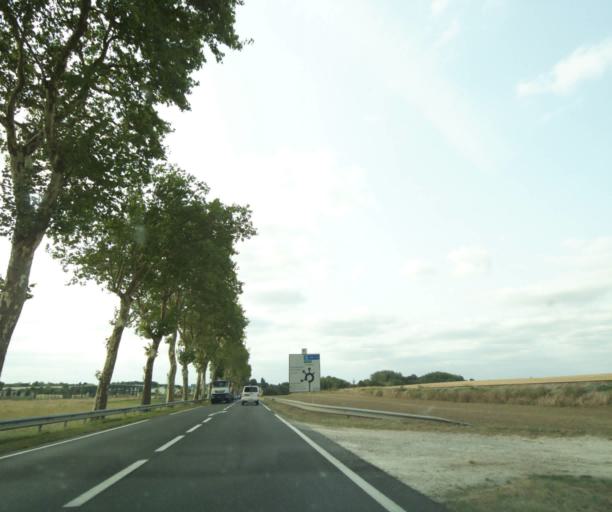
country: FR
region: Centre
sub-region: Departement d'Indre-et-Loire
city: Cormery
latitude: 47.2542
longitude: 0.8460
